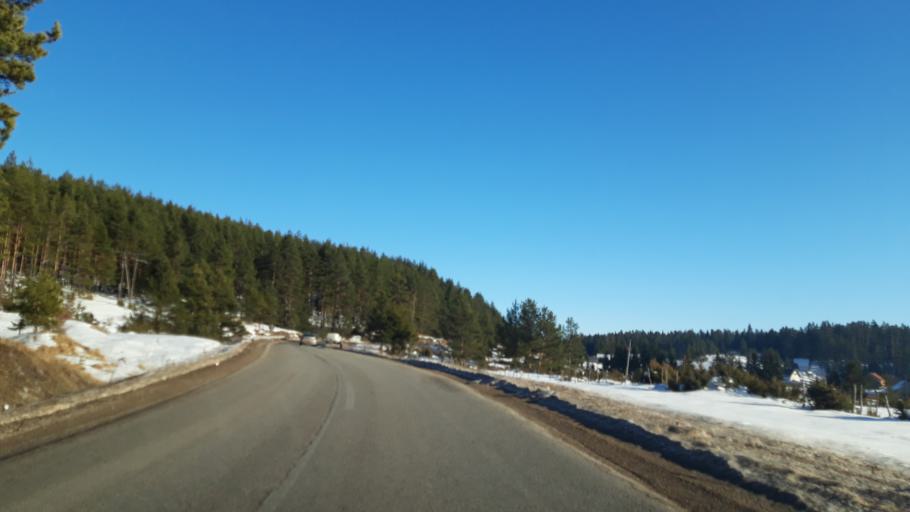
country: BA
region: Republika Srpska
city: Sokolac
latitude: 43.9100
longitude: 18.7037
